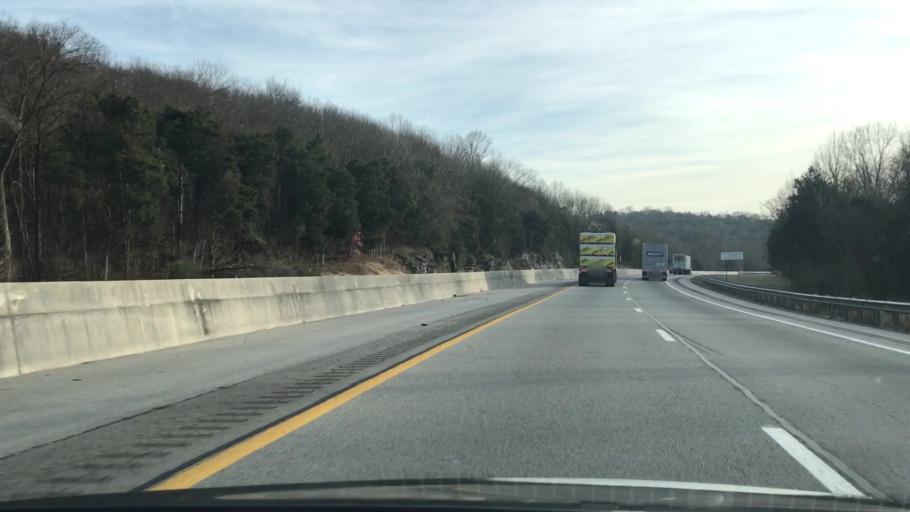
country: US
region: Tennessee
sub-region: Putnam County
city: Lafayette
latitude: 36.1402
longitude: -85.7995
